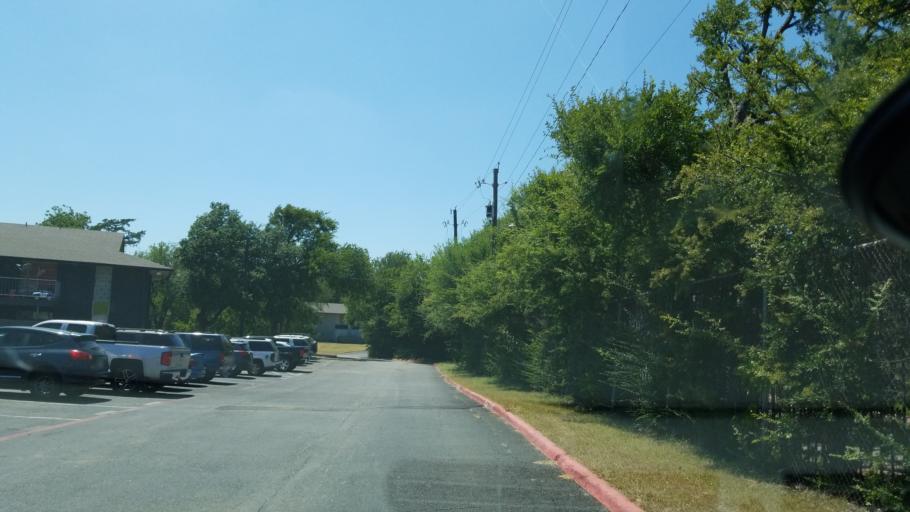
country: US
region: Texas
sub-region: Dallas County
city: Cockrell Hill
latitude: 32.7152
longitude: -96.8873
